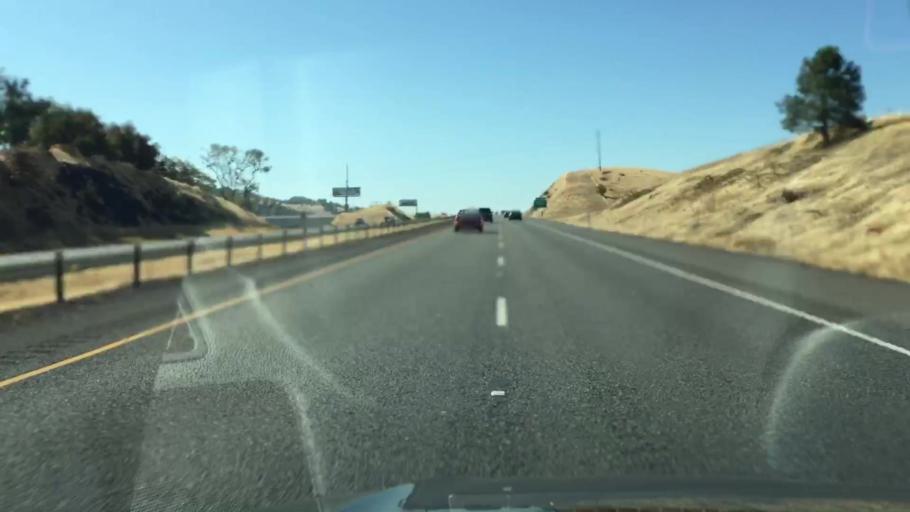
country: US
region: Oregon
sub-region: Douglas County
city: Roseburg North
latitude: 43.3172
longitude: -123.3466
